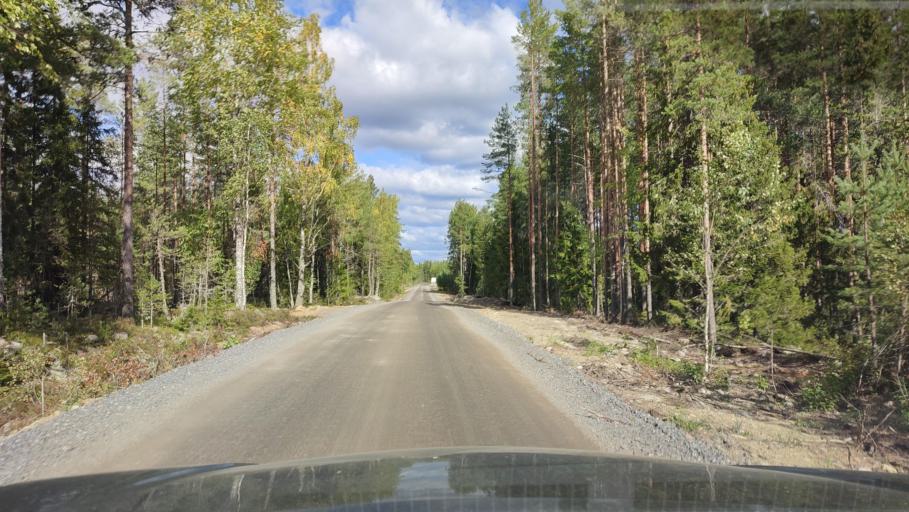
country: FI
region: Southern Ostrobothnia
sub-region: Suupohja
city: Karijoki
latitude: 62.1927
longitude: 21.5884
